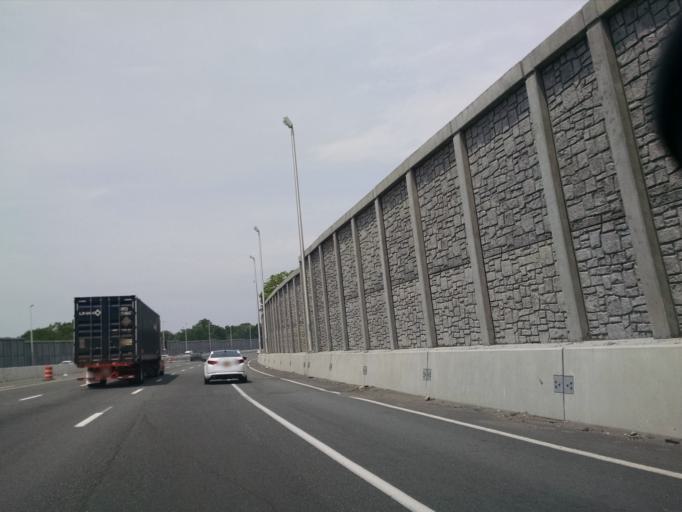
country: US
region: New York
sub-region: Richmond County
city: Bloomfield
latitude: 40.6078
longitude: -74.1459
